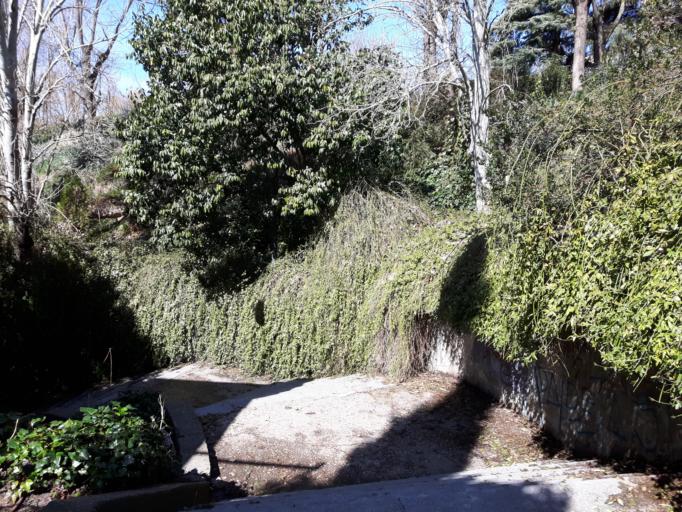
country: ES
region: Madrid
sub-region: Provincia de Madrid
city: Moncloa-Aravaca
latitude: 40.4280
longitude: -3.7217
